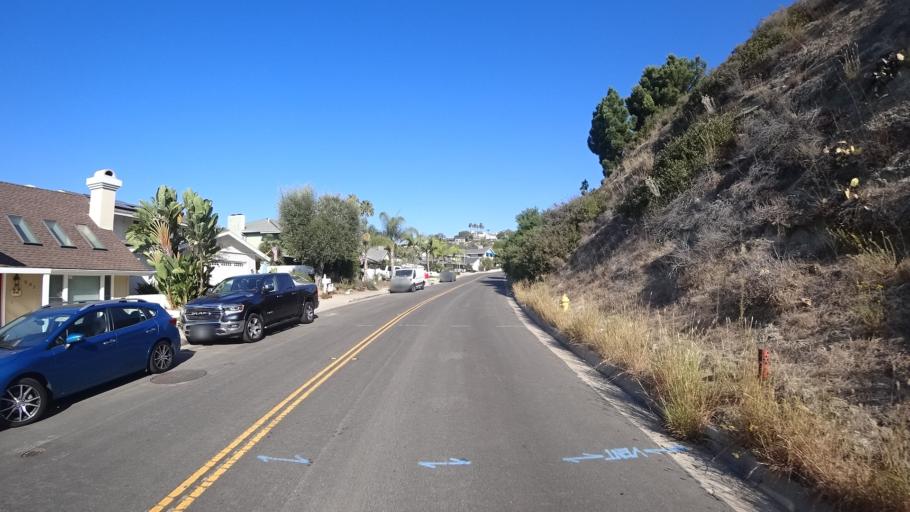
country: US
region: California
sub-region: Orange County
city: San Clemente
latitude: 33.4220
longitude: -117.6015
